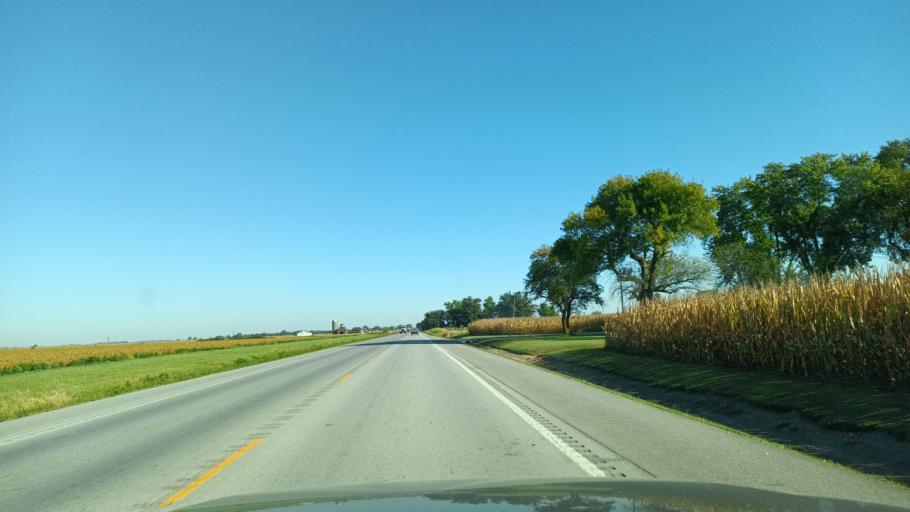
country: US
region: Missouri
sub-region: Montgomery County
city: Wellsville
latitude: 39.2150
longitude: -91.6464
